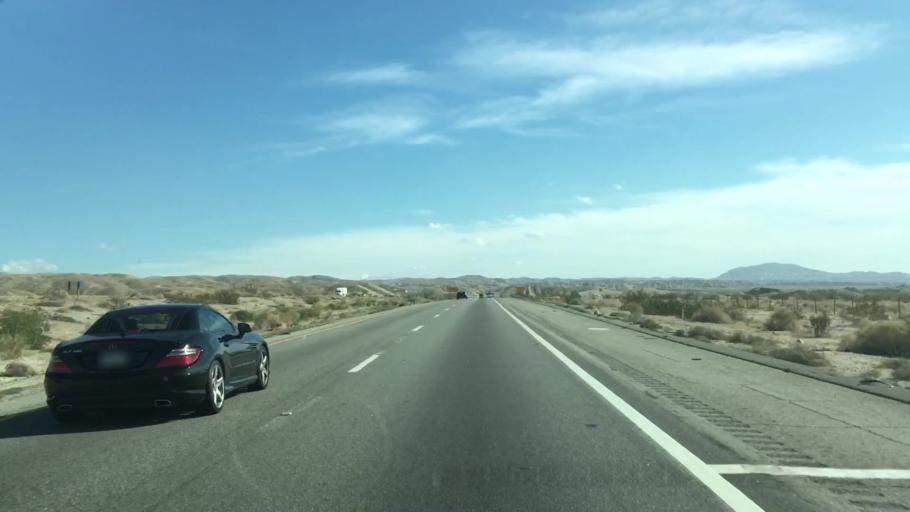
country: US
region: California
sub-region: Riverside County
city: Coachella
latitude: 33.7060
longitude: -116.1382
